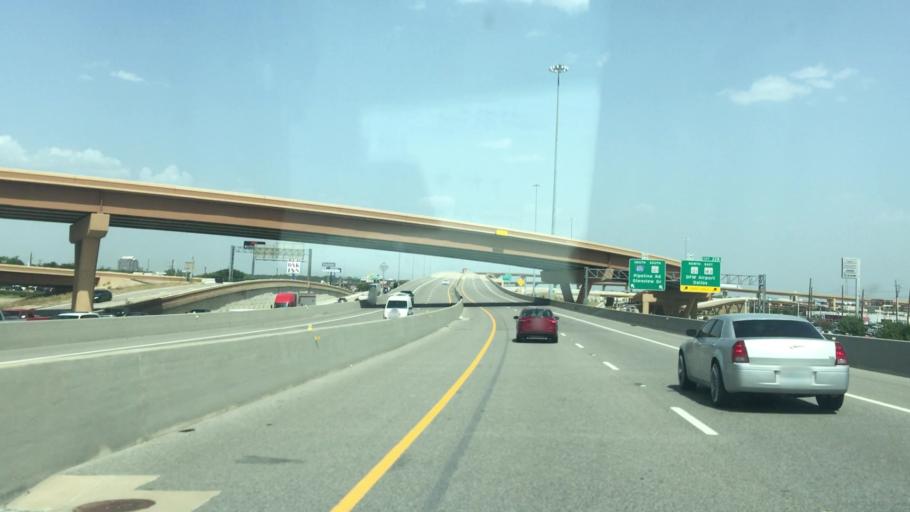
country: US
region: Texas
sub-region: Tarrant County
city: North Richland Hills
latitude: 32.8329
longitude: -97.2147
